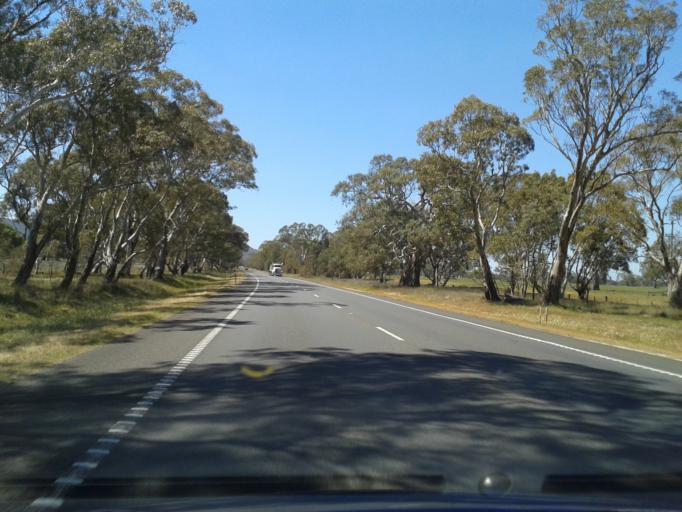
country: AU
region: Victoria
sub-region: Ararat
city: Ararat
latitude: -37.3182
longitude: 143.0473
